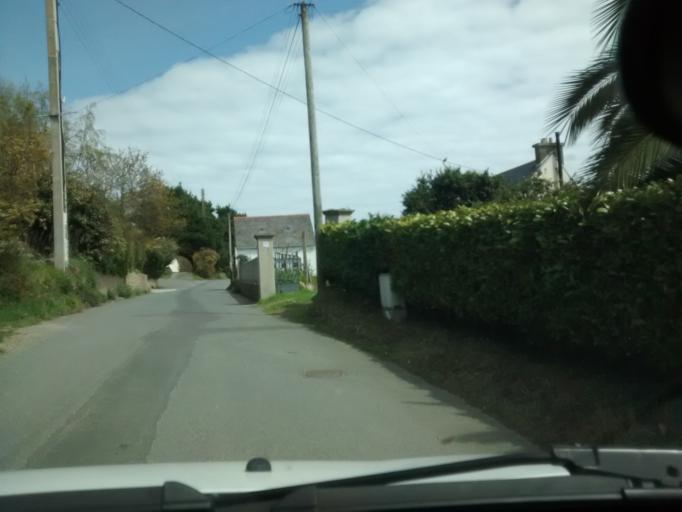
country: FR
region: Brittany
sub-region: Departement des Cotes-d'Armor
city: Ploubazlanec
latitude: 48.7966
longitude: -3.0249
